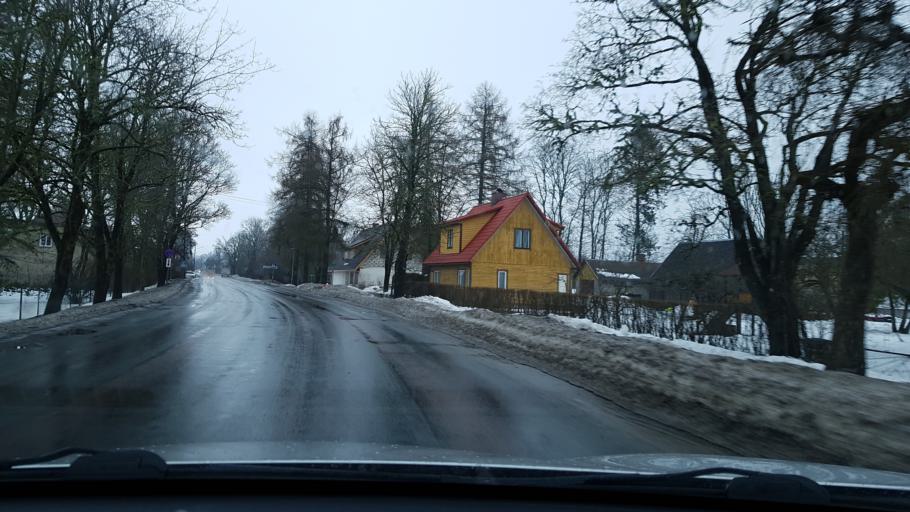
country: EE
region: Raplamaa
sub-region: Maerjamaa vald
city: Marjamaa
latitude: 58.9053
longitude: 24.4288
